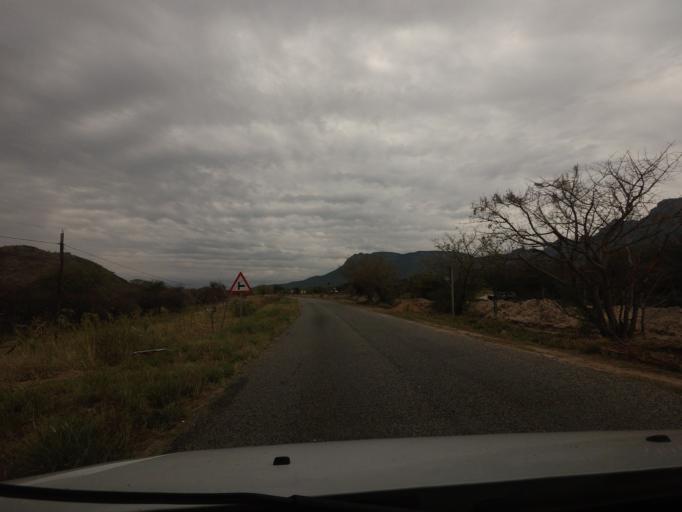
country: ZA
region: Limpopo
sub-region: Mopani District Municipality
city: Hoedspruit
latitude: -24.4980
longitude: 30.8934
